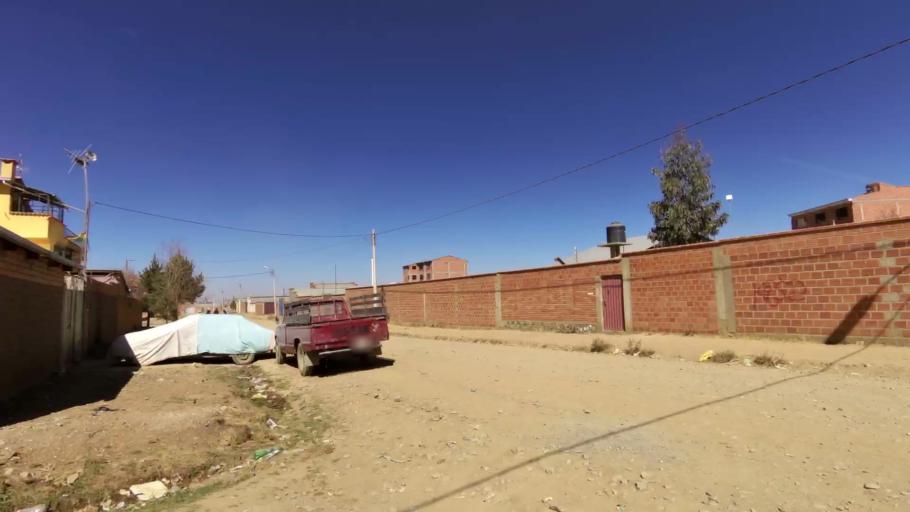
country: BO
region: La Paz
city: La Paz
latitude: -16.5725
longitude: -68.2217
